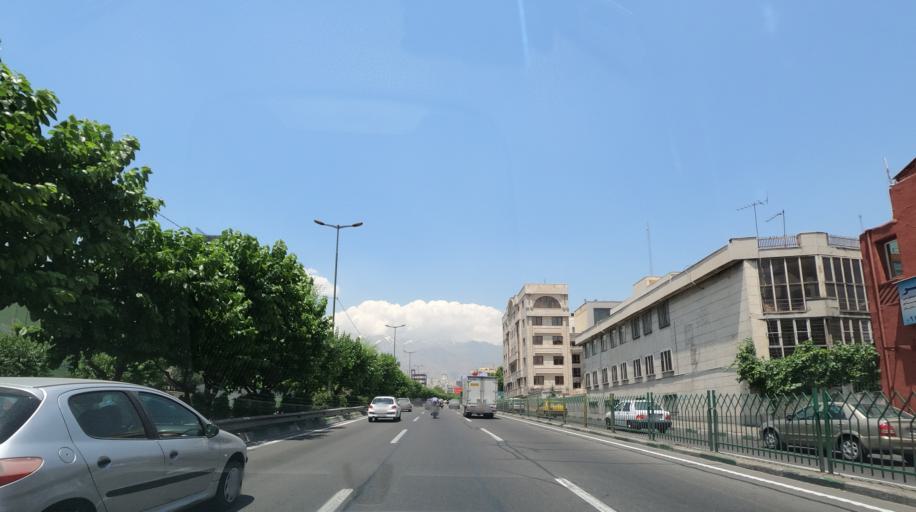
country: IR
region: Tehran
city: Tajrish
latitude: 35.7621
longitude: 51.4210
